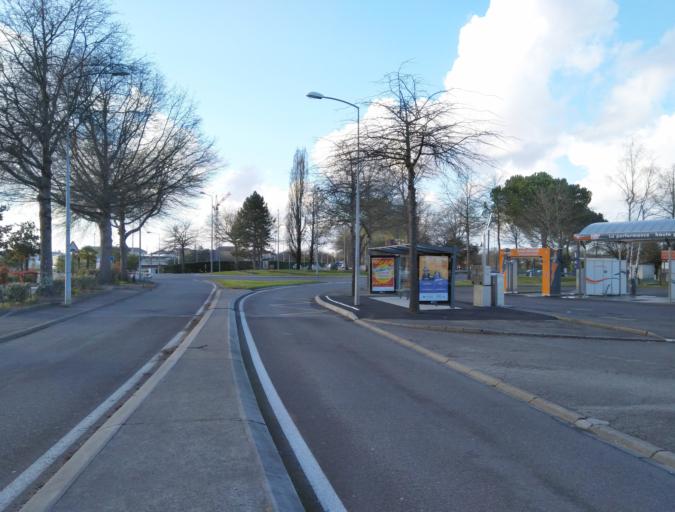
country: FR
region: Aquitaine
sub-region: Departement des Landes
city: Dax
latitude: 43.7100
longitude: -1.0417
